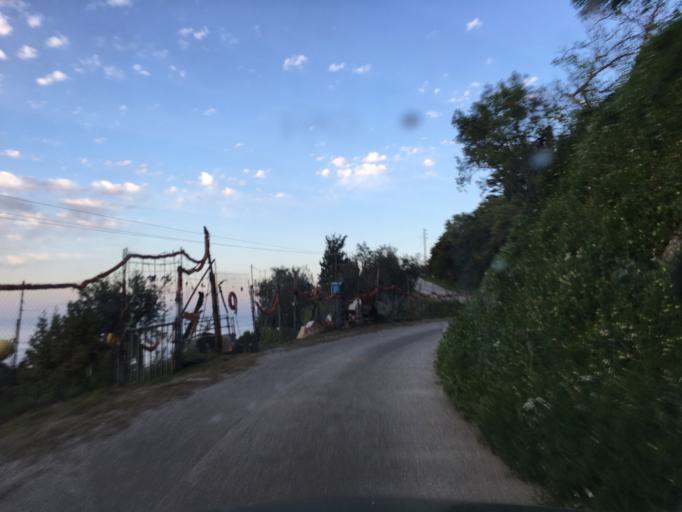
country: GR
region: Thessaly
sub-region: Nomos Magnisias
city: Skopelos
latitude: 39.1812
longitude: 23.6195
